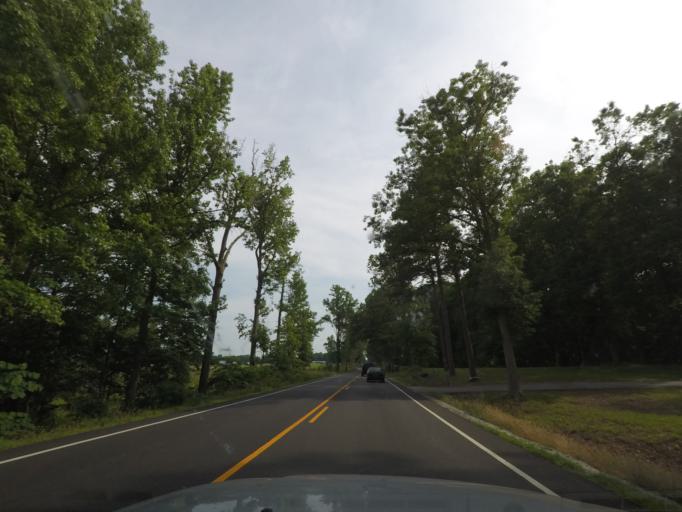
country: US
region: Virginia
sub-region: Prince Edward County
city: Hampden Sydney
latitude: 37.1493
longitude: -78.4407
